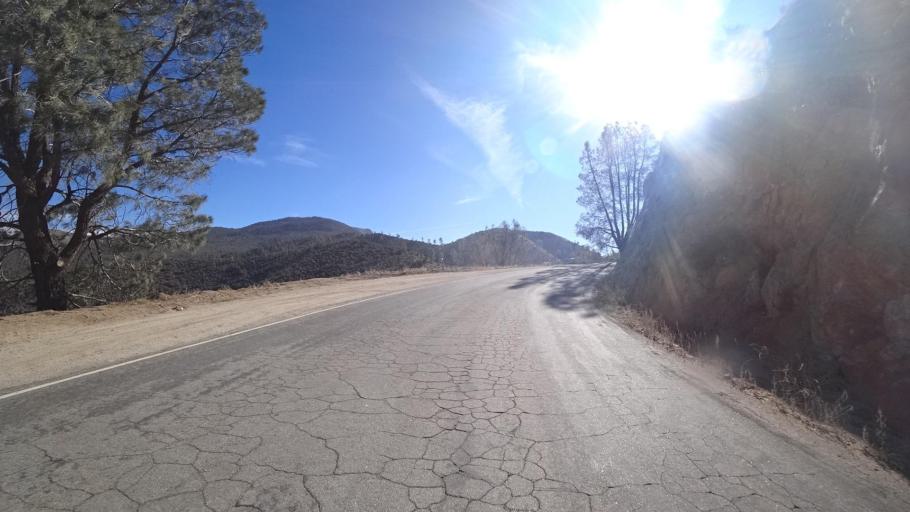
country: US
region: California
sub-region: Kern County
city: Bodfish
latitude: 35.5786
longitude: -118.5048
